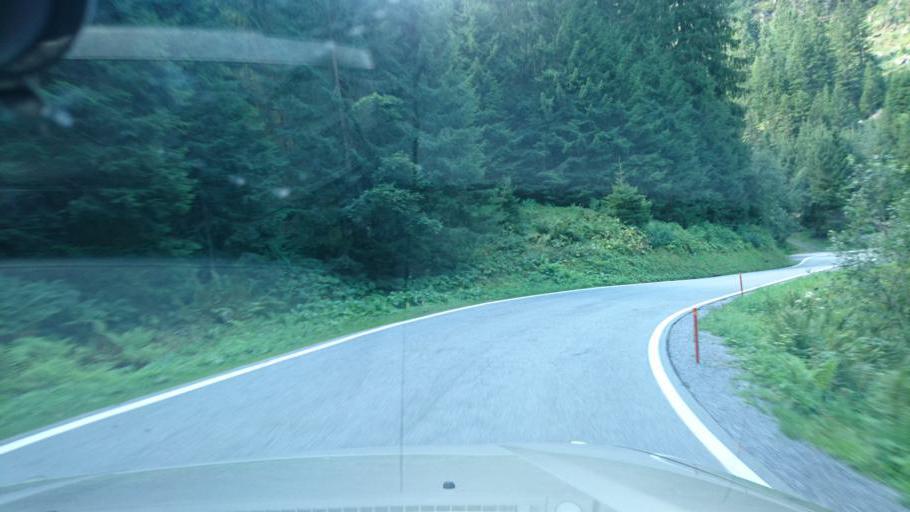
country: AT
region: Vorarlberg
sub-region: Politischer Bezirk Bludenz
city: Gaschurn
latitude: 46.9526
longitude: 10.0726
